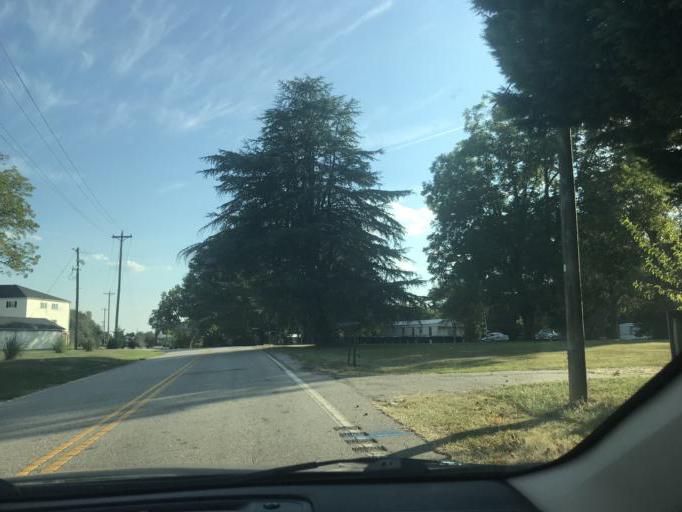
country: US
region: South Carolina
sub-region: Cherokee County
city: Gaffney
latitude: 35.0992
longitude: -81.6892
